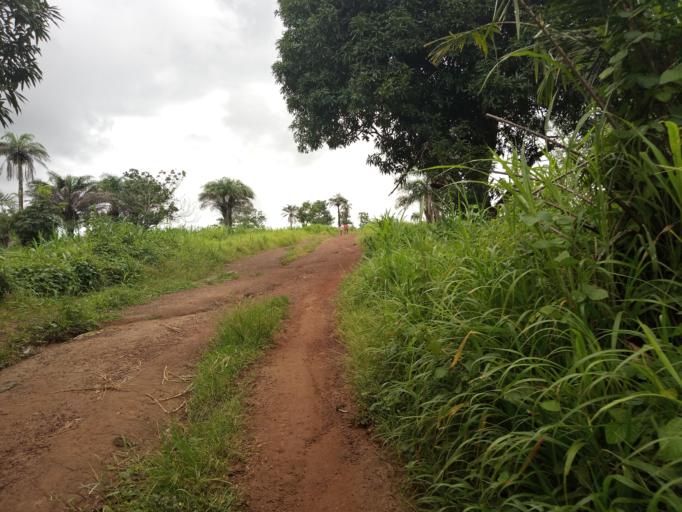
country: SL
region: Northern Province
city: Kamakwie
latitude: 9.4885
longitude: -12.2456
